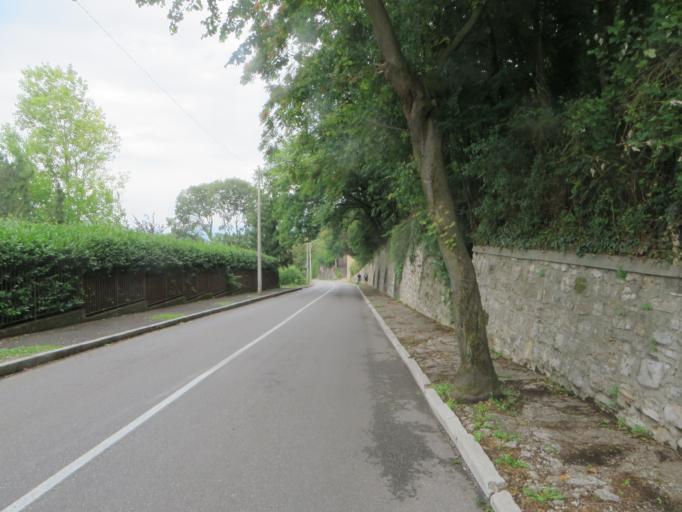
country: IT
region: Lombardy
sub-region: Provincia di Brescia
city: Brescia
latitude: 45.5410
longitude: 10.2404
